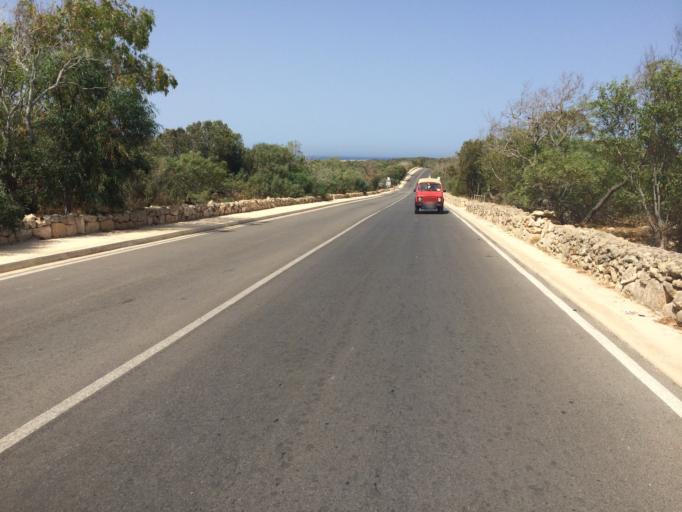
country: MT
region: Il-Mellieha
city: Mellieha
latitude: 35.9789
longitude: 14.3520
